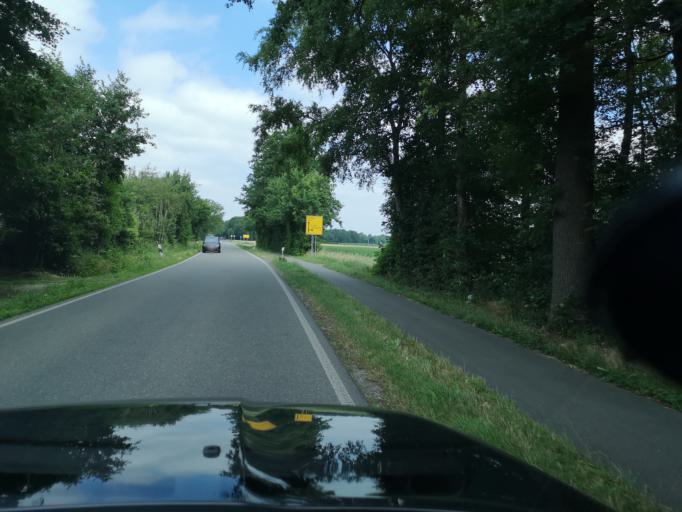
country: DE
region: North Rhine-Westphalia
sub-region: Regierungsbezirk Munster
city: Rhede
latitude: 51.8845
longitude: 6.6851
